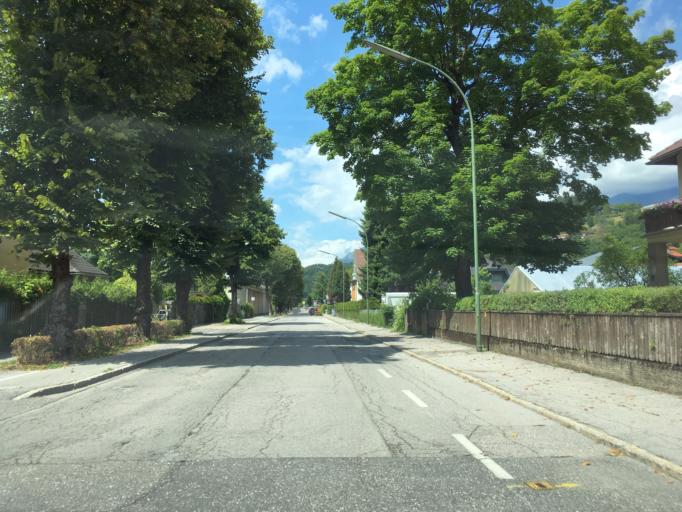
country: AT
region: Carinthia
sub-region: Politischer Bezirk Spittal an der Drau
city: Spittal an der Drau
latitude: 46.8020
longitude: 13.4931
